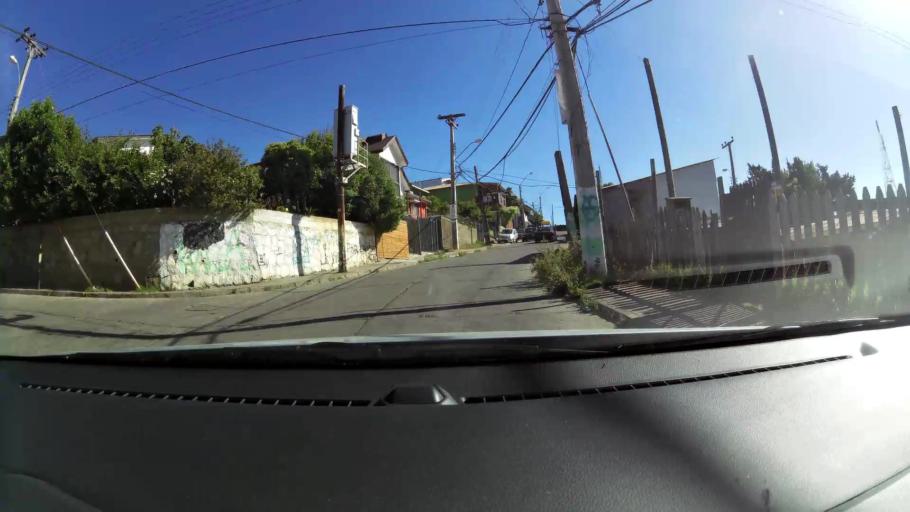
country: CL
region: Valparaiso
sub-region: Provincia de Valparaiso
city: Vina del Mar
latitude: -33.0435
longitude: -71.5627
